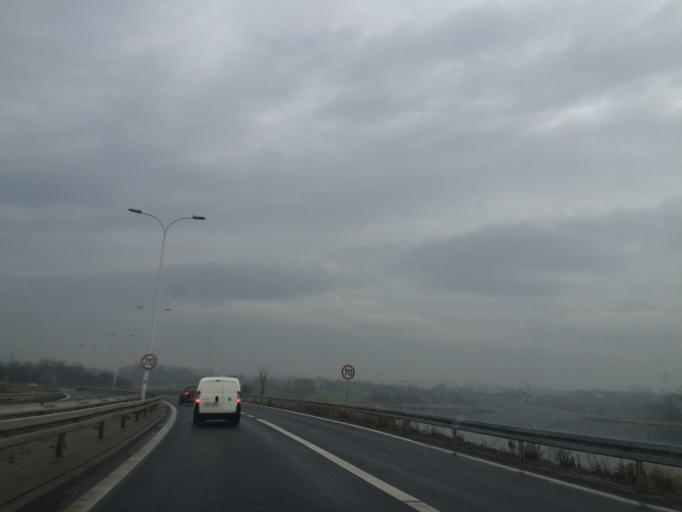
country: PL
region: Silesian Voivodeship
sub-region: Powiat tarnogorski
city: Radzionkow
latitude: 50.3669
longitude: 18.8738
